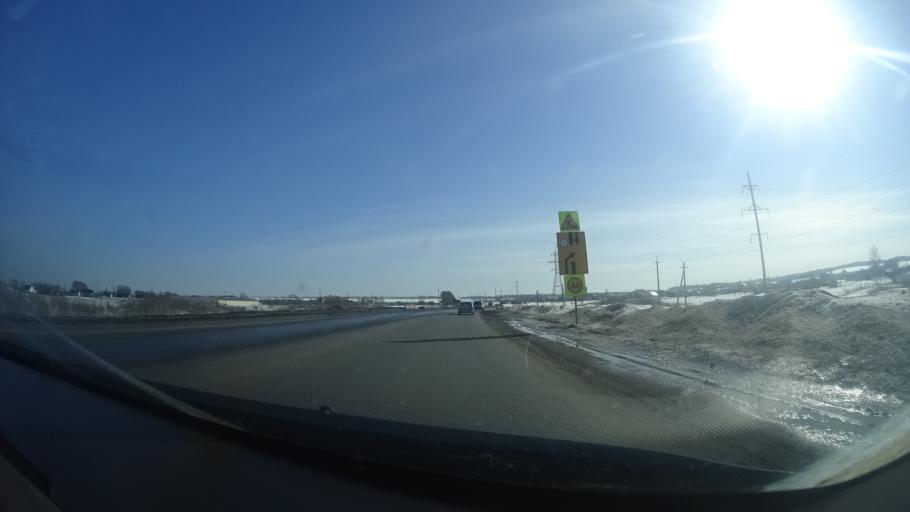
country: RU
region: Bashkortostan
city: Mikhaylovka
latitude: 54.8715
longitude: 55.7373
